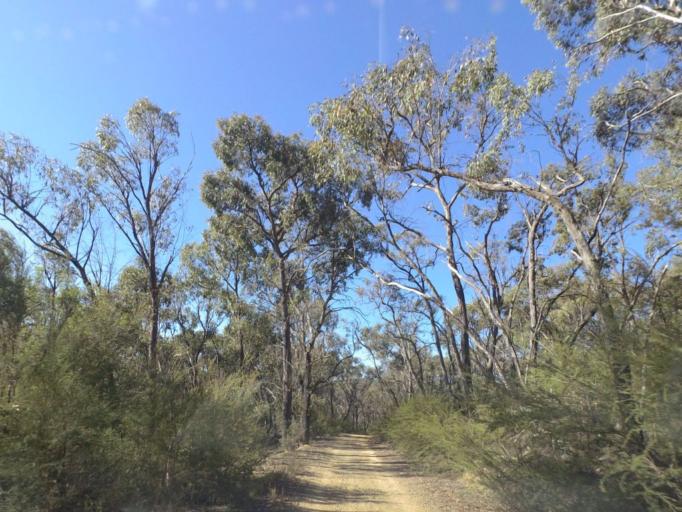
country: AU
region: Victoria
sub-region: Murrindindi
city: Kinglake West
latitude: -37.4664
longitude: 145.3656
